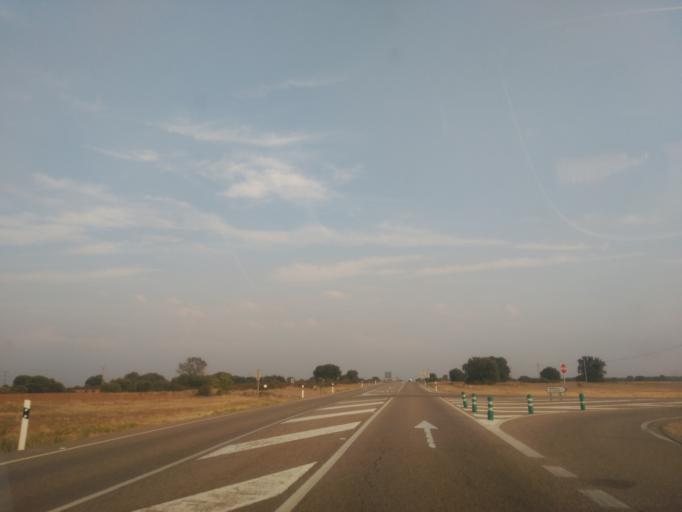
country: ES
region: Castille and Leon
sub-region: Provincia de Zamora
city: Perilla de Castro
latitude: 41.7358
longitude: -5.8281
